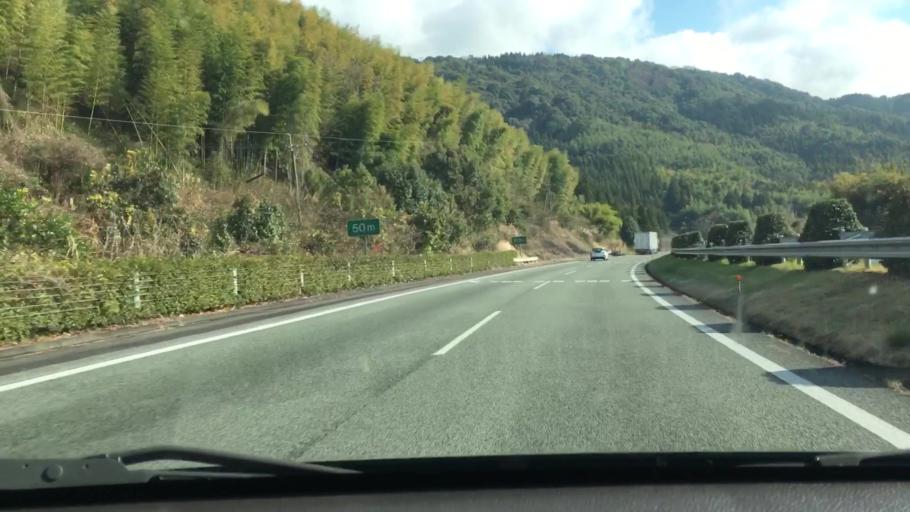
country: JP
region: Kumamoto
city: Matsubase
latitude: 32.6160
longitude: 130.7220
